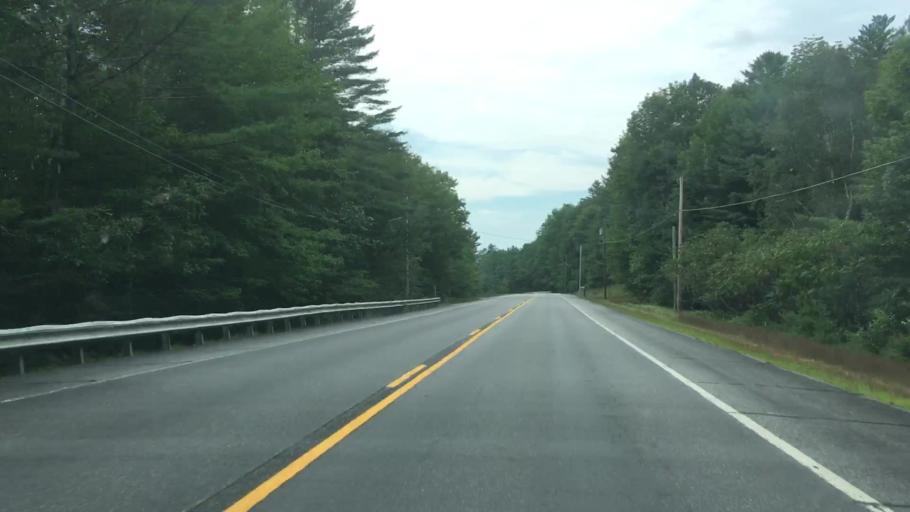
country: US
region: Maine
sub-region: Oxford County
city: Bethel
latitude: 44.4870
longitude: -70.7672
